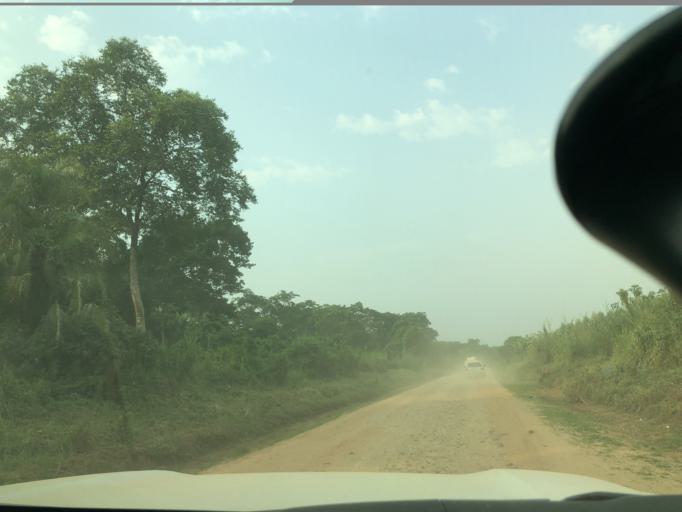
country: UG
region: Western Region
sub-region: Kasese District
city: Margherita
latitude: 0.2958
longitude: 29.6627
